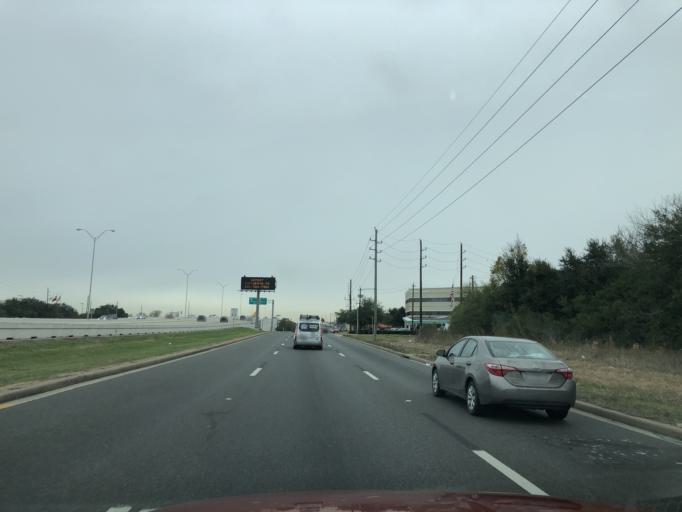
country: US
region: Texas
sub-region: Fort Bend County
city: Missouri City
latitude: 29.6418
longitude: -95.5357
